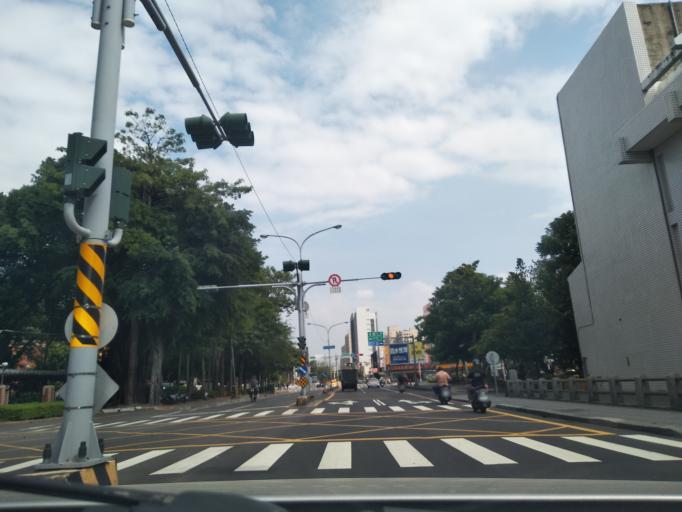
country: TW
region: Taiwan
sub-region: Tainan
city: Tainan
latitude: 23.0042
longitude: 120.2124
